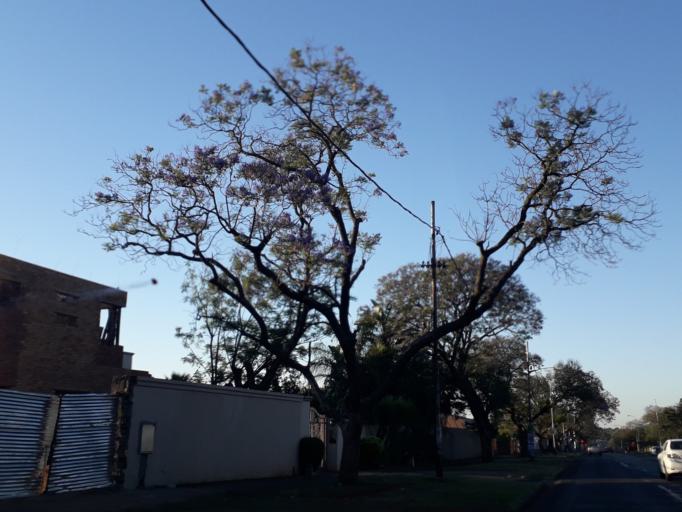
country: ZA
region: Gauteng
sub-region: City of Johannesburg Metropolitan Municipality
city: Johannesburg
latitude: -26.1541
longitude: 28.0106
